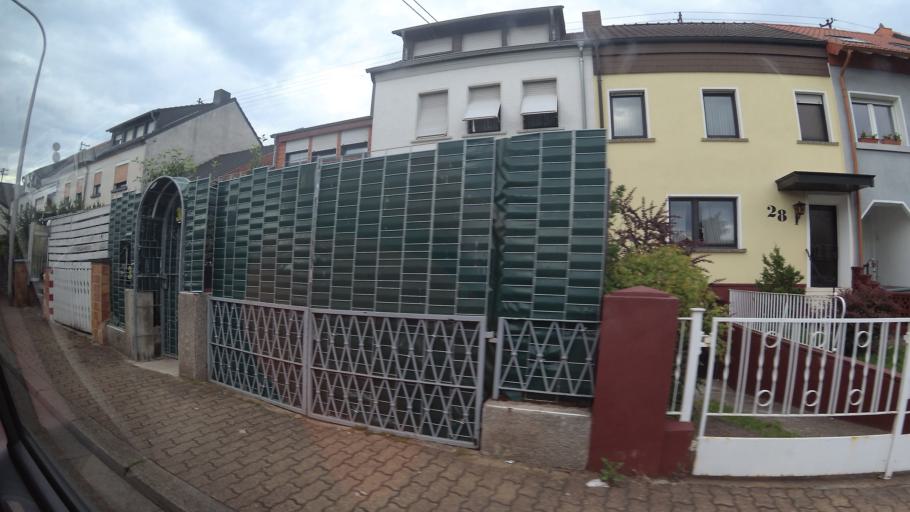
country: DE
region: Saarland
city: Saarlouis
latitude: 49.3323
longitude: 6.7539
